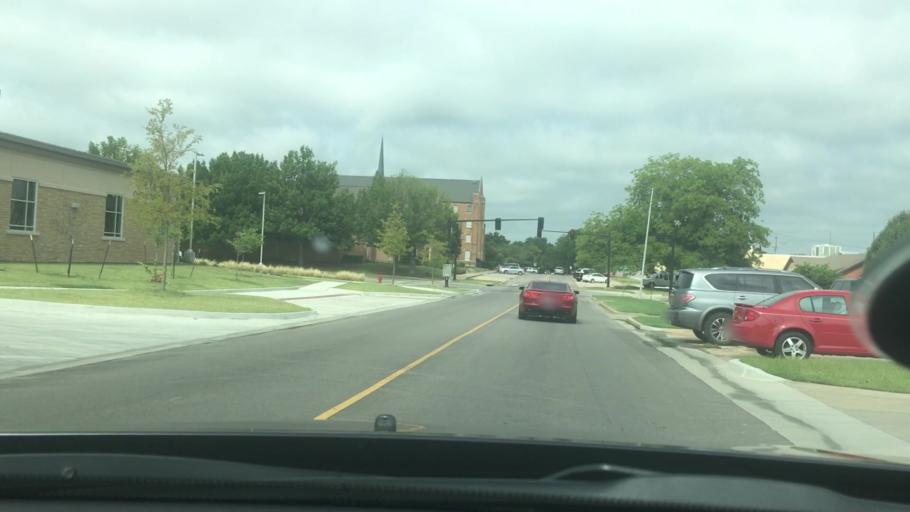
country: US
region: Oklahoma
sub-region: Pontotoc County
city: Ada
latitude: 34.7713
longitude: -96.6776
